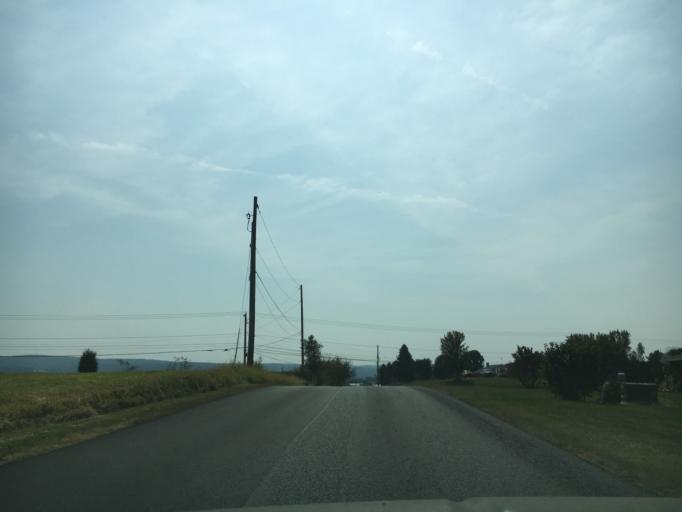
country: US
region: Pennsylvania
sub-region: Berks County
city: Topton
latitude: 40.5406
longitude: -75.7168
